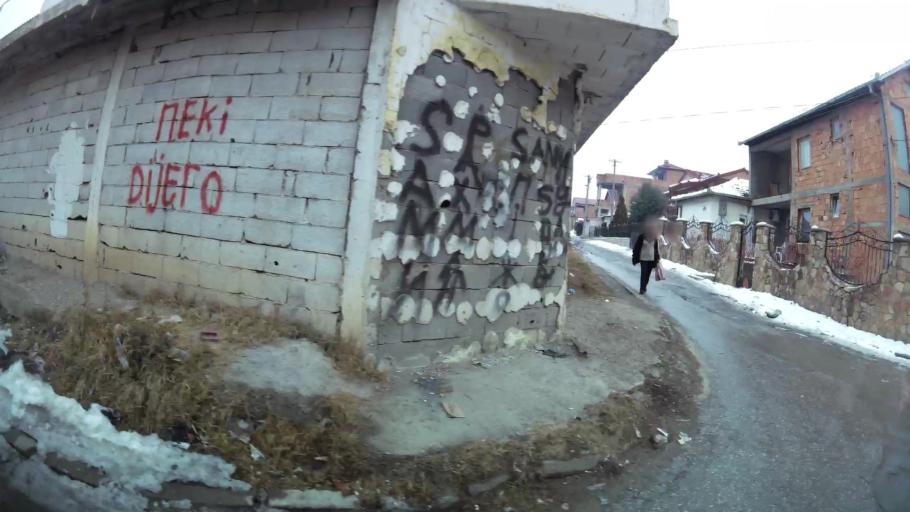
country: MK
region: Suto Orizari
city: Suto Orizare
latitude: 42.0386
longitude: 21.4218
